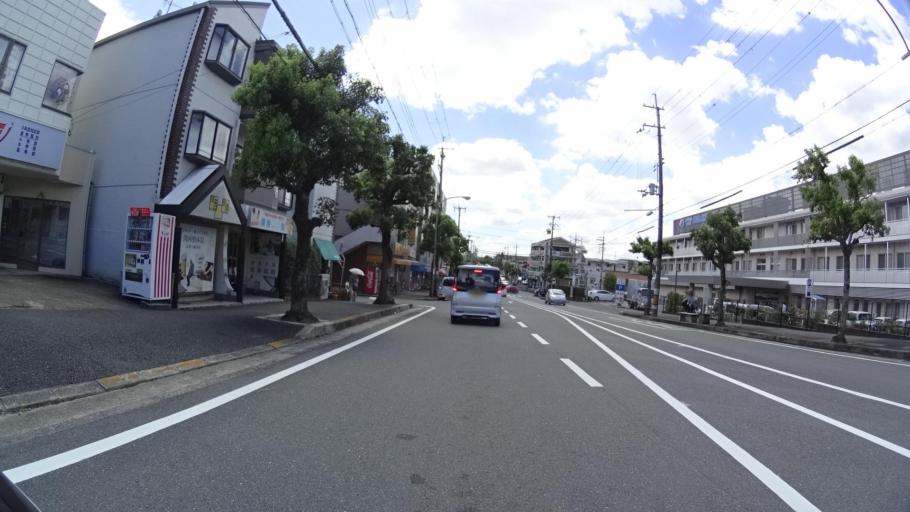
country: JP
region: Kyoto
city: Yawata
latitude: 34.8619
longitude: 135.6943
